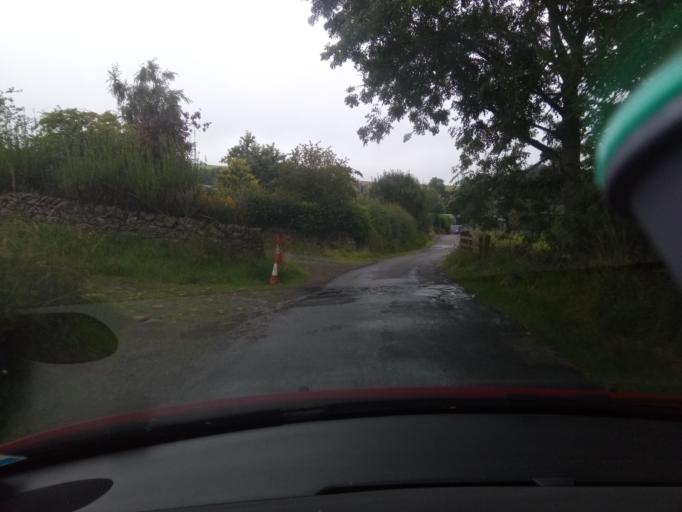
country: GB
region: Scotland
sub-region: The Scottish Borders
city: Galashiels
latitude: 55.7033
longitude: -2.8930
